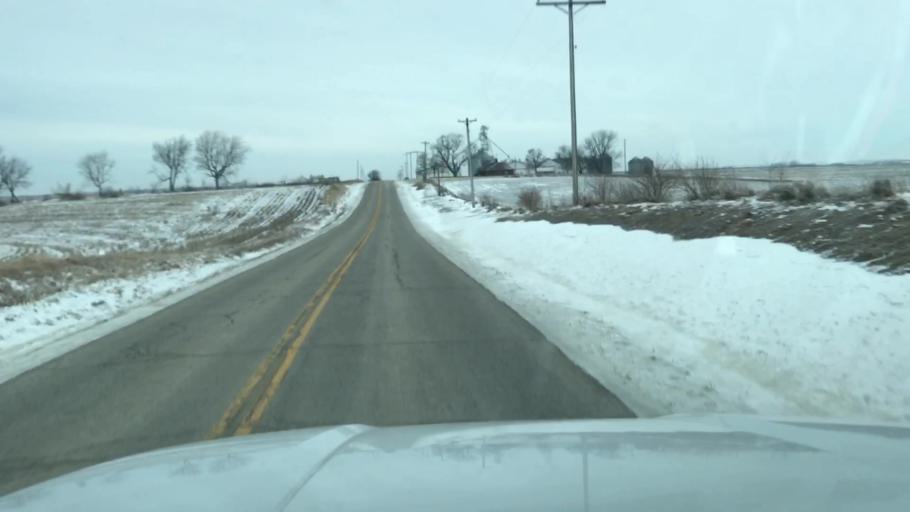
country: US
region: Missouri
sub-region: Andrew County
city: Savannah
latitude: 40.0248
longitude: -94.9340
